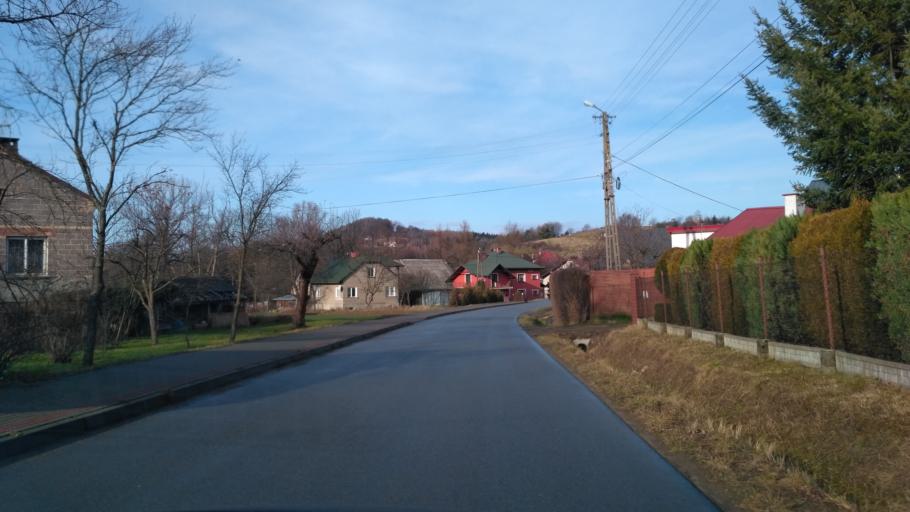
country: PL
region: Subcarpathian Voivodeship
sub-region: Powiat krosnienski
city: Korczyna
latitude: 49.7197
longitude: 21.8084
